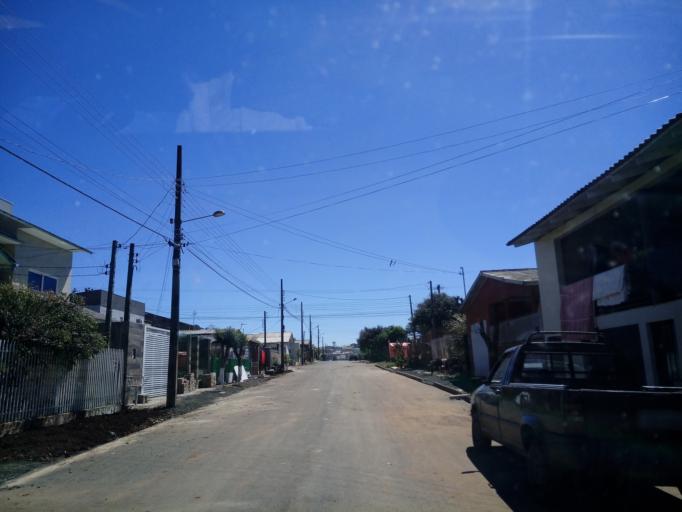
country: BR
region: Santa Catarina
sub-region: Chapeco
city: Chapeco
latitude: -27.0942
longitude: -52.6727
